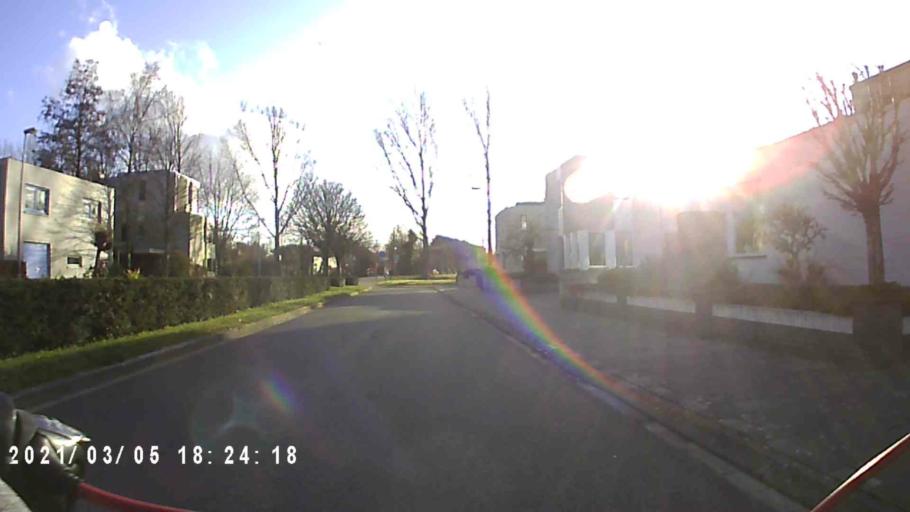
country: NL
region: Groningen
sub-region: Gemeente Groningen
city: Korrewegwijk
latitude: 53.2410
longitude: 6.5761
